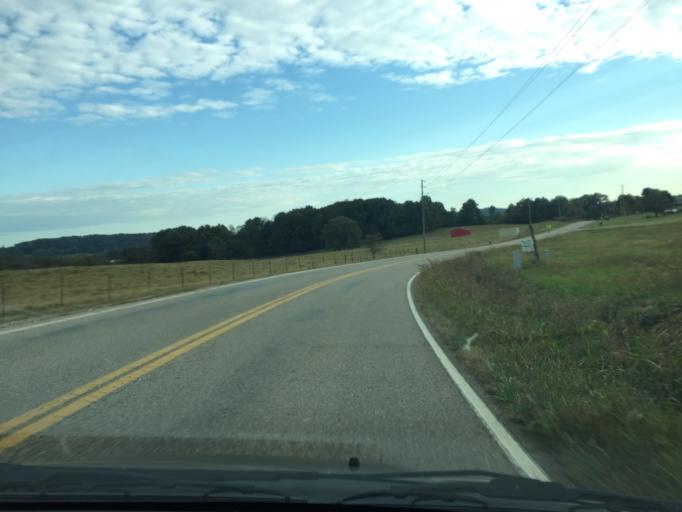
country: US
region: Tennessee
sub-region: Monroe County
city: Sweetwater
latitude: 35.6345
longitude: -84.5044
